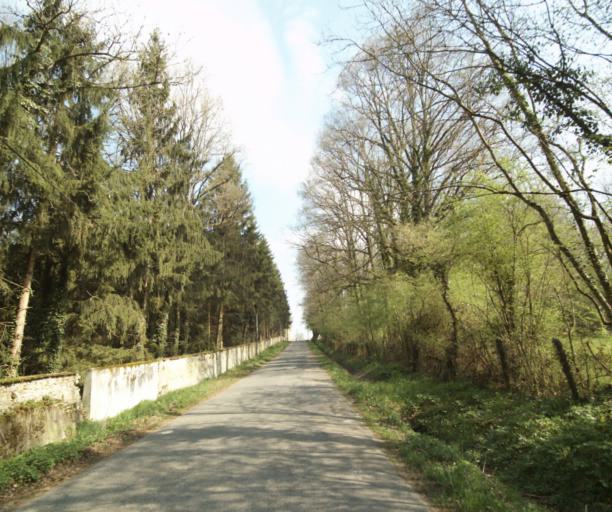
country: FR
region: Bourgogne
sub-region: Departement de Saone-et-Loire
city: Palinges
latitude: 46.5193
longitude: 4.2109
